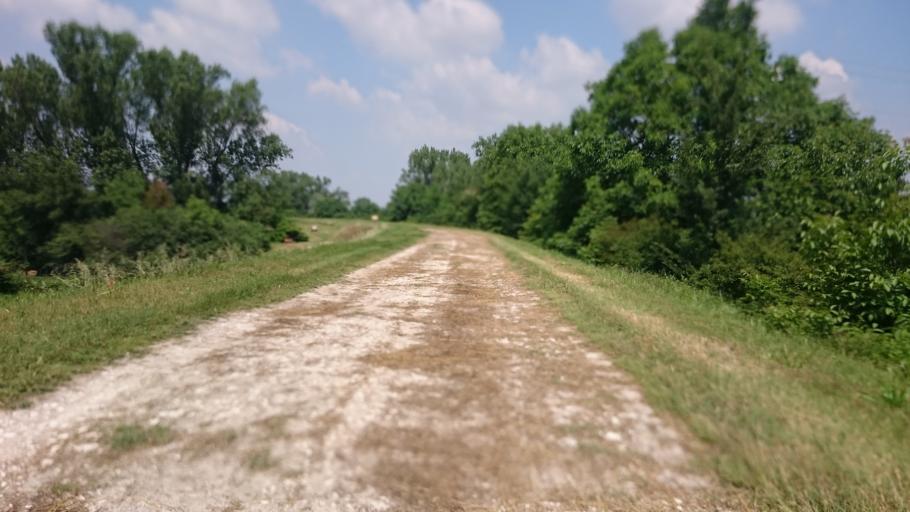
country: IT
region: Lombardy
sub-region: Provincia di Mantova
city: Bagnolo San Vito
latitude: 45.1032
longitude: 10.8853
